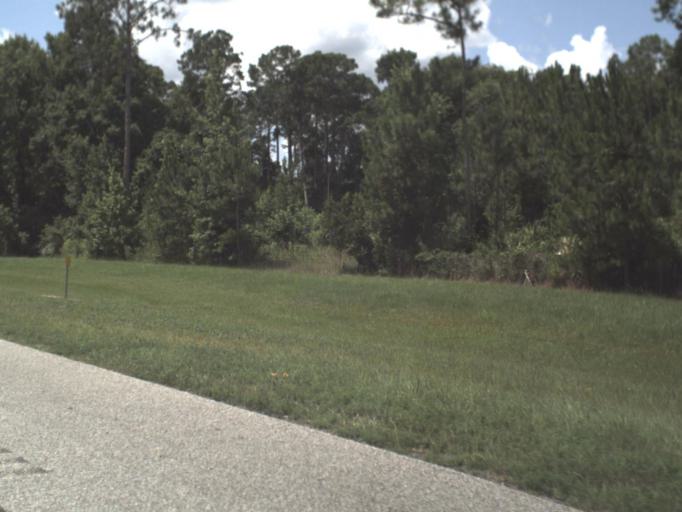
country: US
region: Florida
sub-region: Saint Johns County
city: Saint Augustine Shores
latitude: 29.6880
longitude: -81.3227
